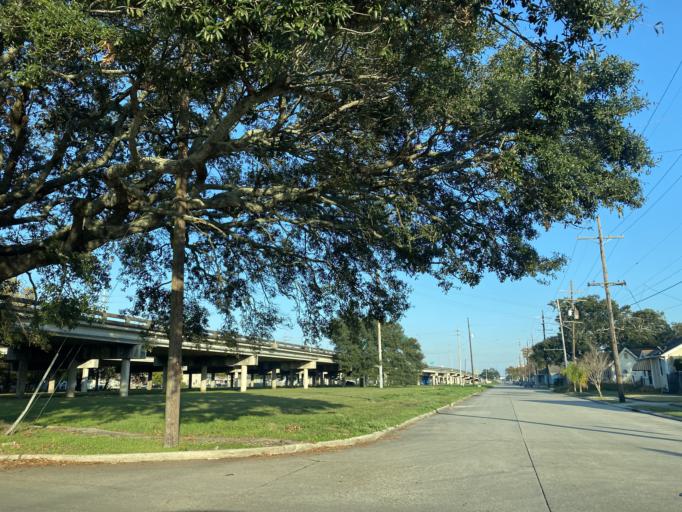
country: US
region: Louisiana
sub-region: Orleans Parish
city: New Orleans
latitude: 29.9905
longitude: -90.0633
